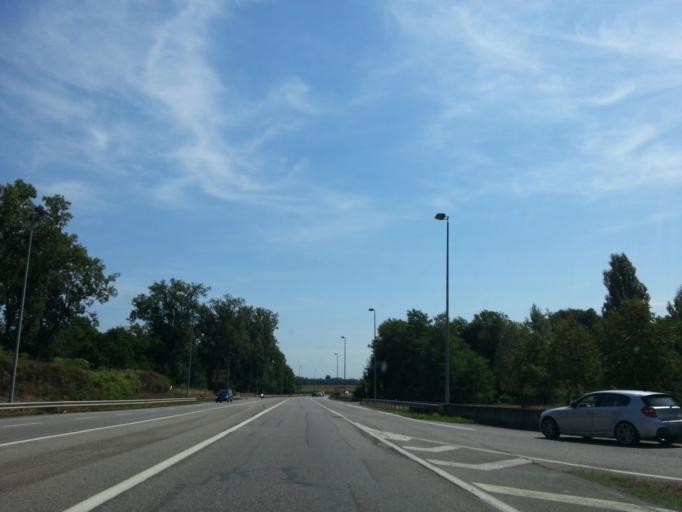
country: FR
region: Alsace
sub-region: Departement du Haut-Rhin
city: Horbourg-Wihr
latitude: 48.0679
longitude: 7.3857
